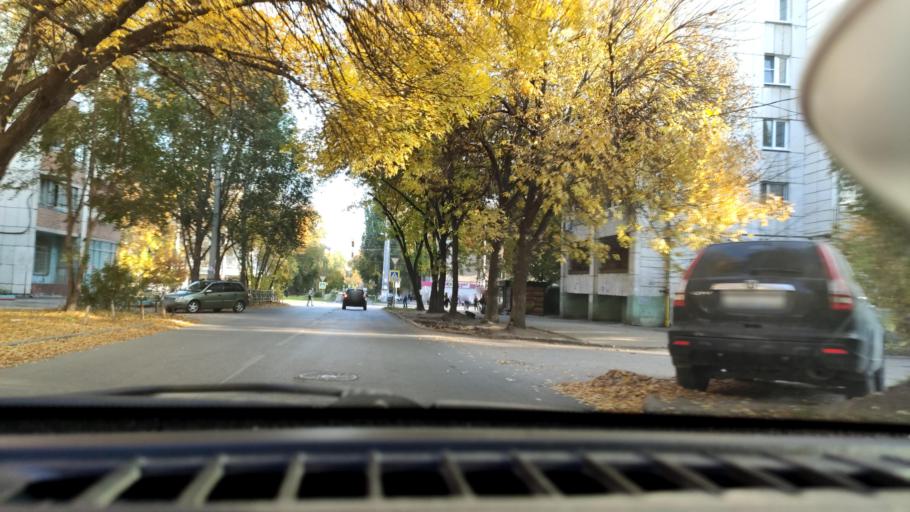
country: RU
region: Samara
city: Petra-Dubrava
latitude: 53.2317
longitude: 50.2710
